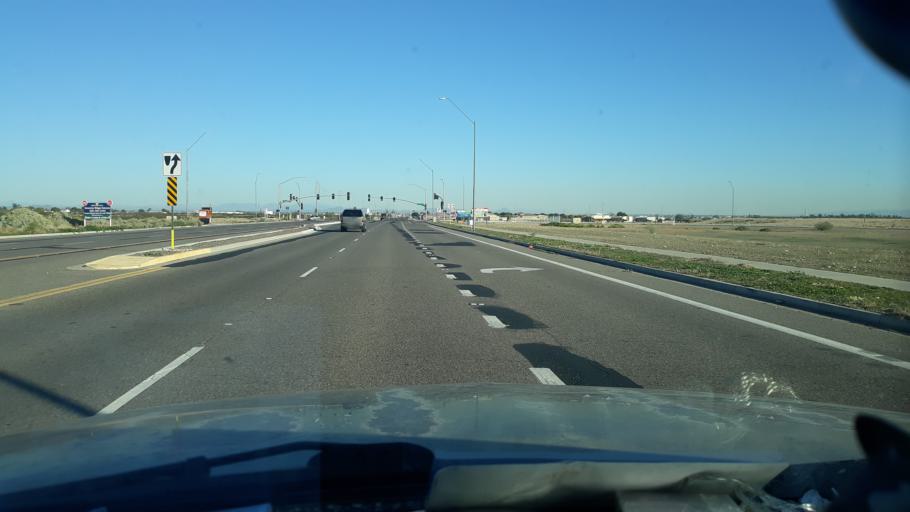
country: US
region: Arizona
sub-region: Maricopa County
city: Citrus Park
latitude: 33.5661
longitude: -112.4465
